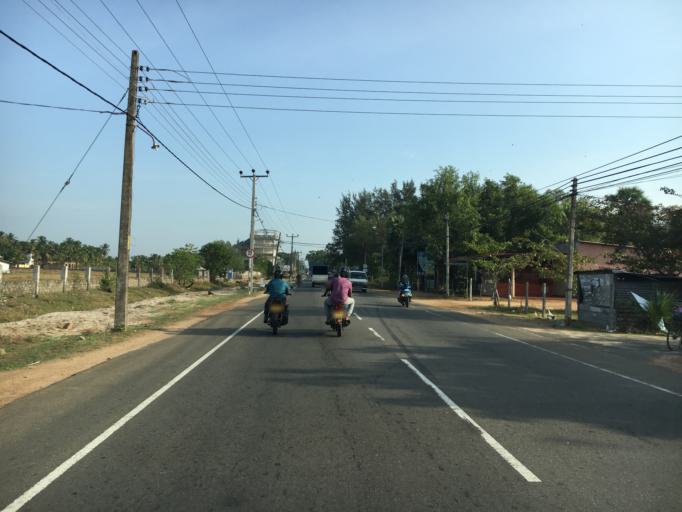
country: LK
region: Eastern Province
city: Eravur Town
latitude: 7.9035
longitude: 81.5349
